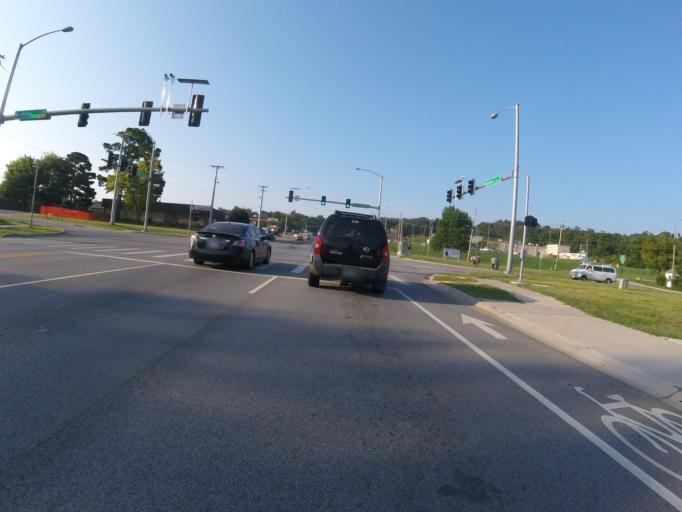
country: US
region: Arkansas
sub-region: Washington County
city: Fayetteville
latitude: 36.0803
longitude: -94.1753
